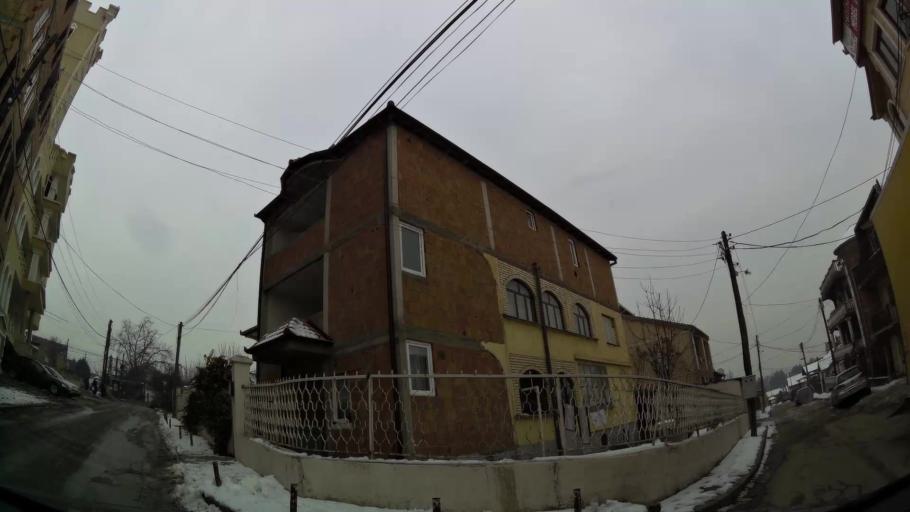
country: MK
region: Suto Orizari
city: Suto Orizare
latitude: 42.0343
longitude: 21.4260
